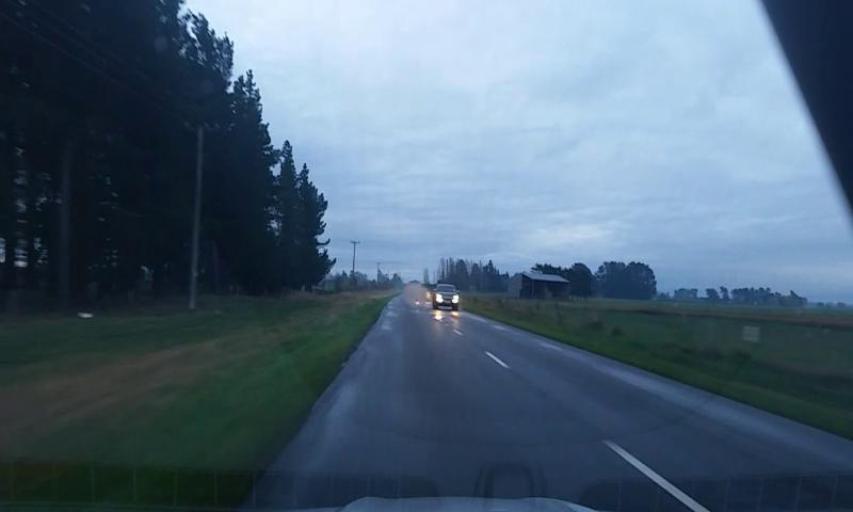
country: NZ
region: Canterbury
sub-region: Ashburton District
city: Rakaia
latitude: -43.7585
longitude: 171.9666
